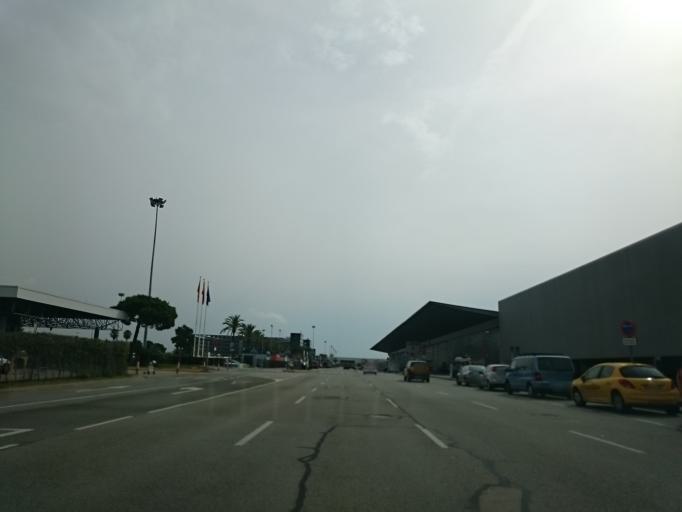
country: ES
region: Catalonia
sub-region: Provincia de Barcelona
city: El Prat de Llobregat
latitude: 41.3029
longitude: 2.0752
